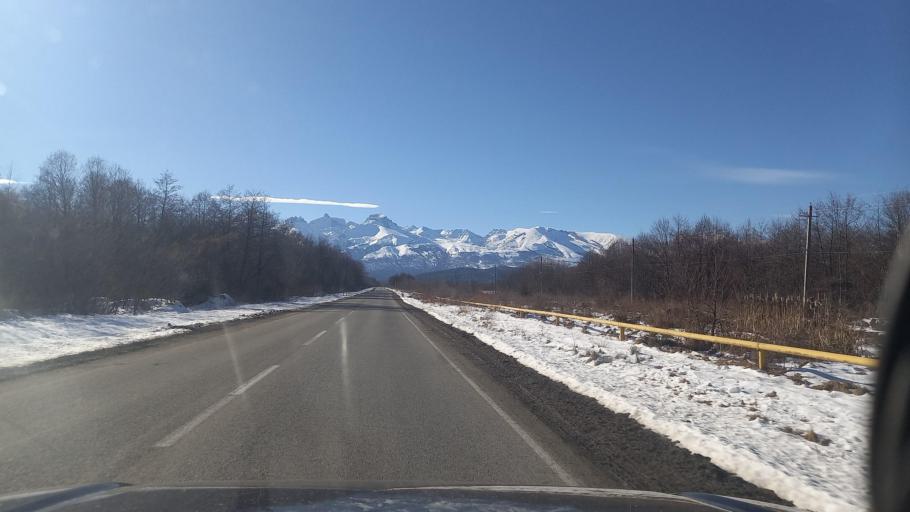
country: RU
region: North Ossetia
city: Chikola
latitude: 43.1602
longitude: 43.8503
